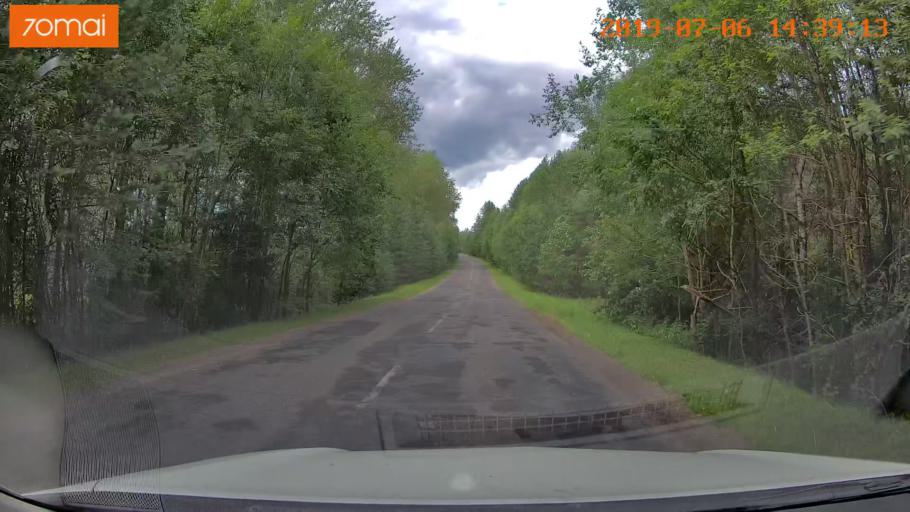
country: BY
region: Minsk
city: Ivyanyets
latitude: 53.9144
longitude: 26.6922
